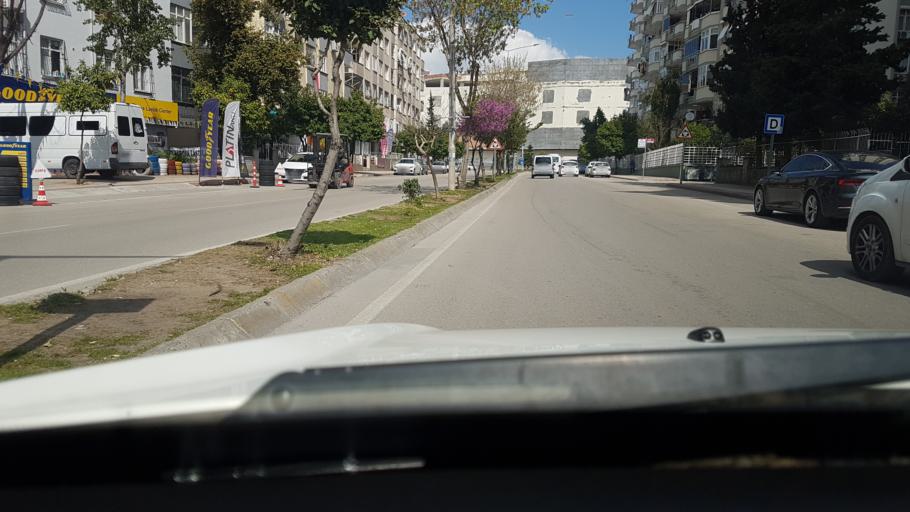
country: TR
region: Adana
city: Adana
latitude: 37.0411
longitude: 35.3021
